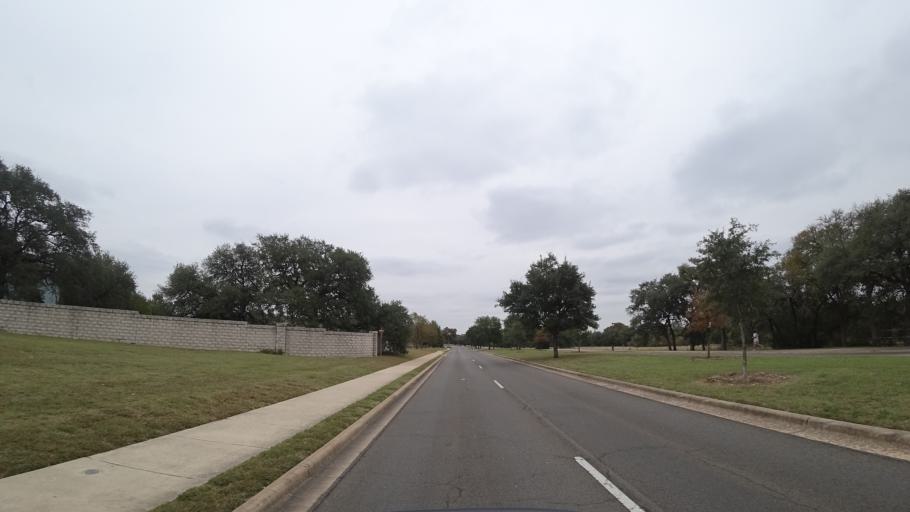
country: US
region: Texas
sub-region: Travis County
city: Shady Hollow
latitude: 30.2073
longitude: -97.8881
